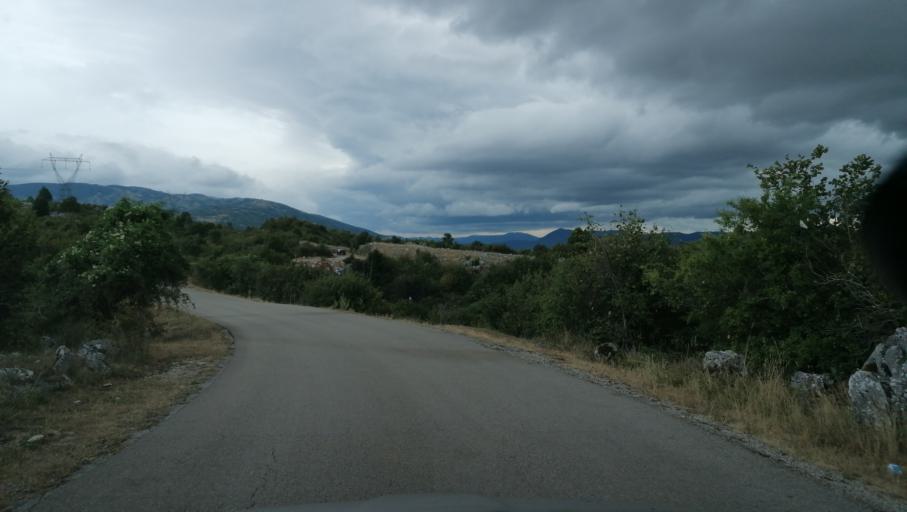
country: BA
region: Republika Srpska
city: Gacko
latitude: 43.1567
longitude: 18.5660
